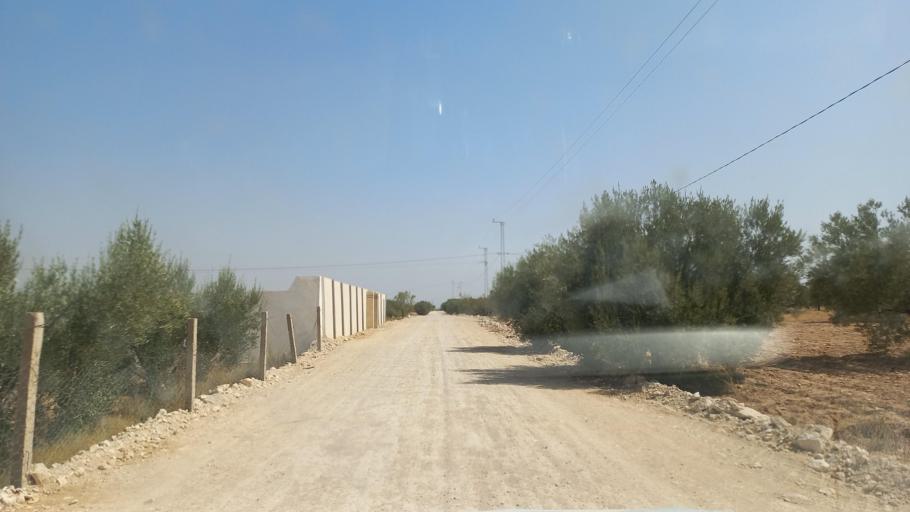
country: TN
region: Al Qasrayn
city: Kasserine
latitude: 35.2594
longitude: 9.0115
